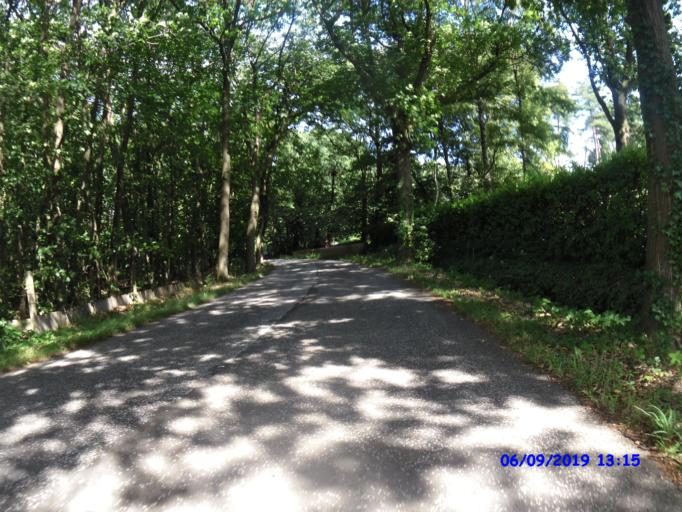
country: BE
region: Flanders
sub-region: Provincie Antwerpen
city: Geel
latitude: 51.2096
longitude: 5.0392
